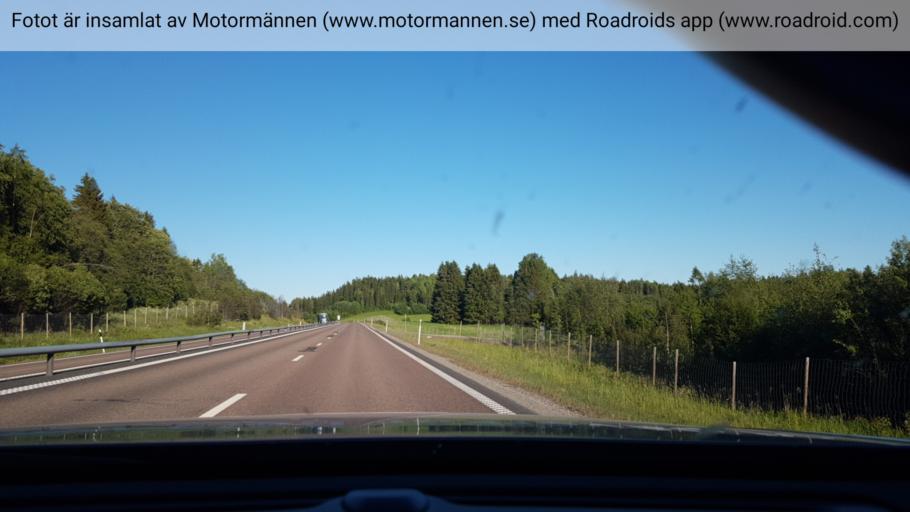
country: SE
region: Vaesternorrland
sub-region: OErnskoeldsviks Kommun
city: Ornskoldsvik
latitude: 63.3129
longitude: 18.8199
